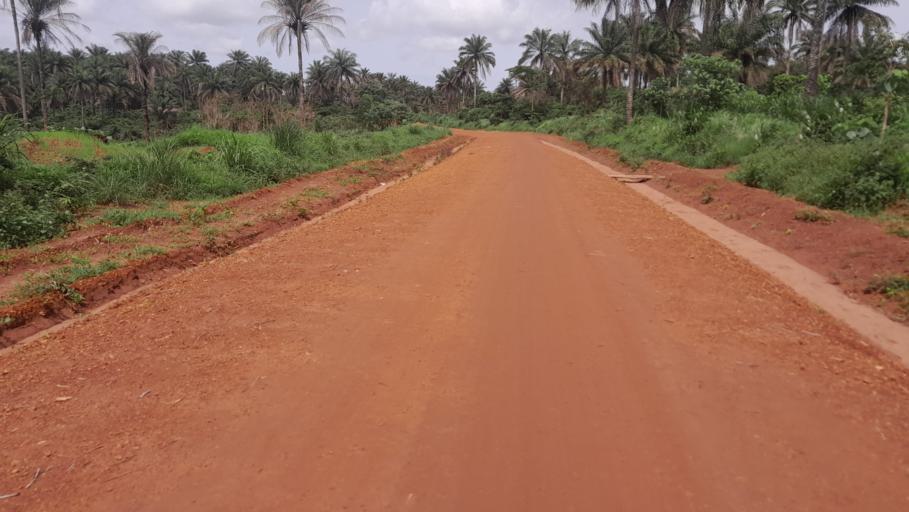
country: GN
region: Boke
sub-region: Boffa
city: Boffa
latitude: 10.0303
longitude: -13.8806
